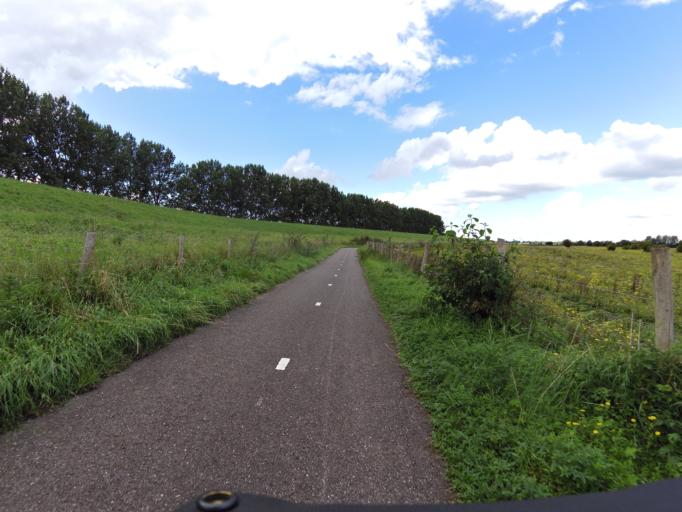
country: NL
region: North Brabant
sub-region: Gemeente Steenbergen
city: Dinteloord
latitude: 51.6847
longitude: 4.3626
